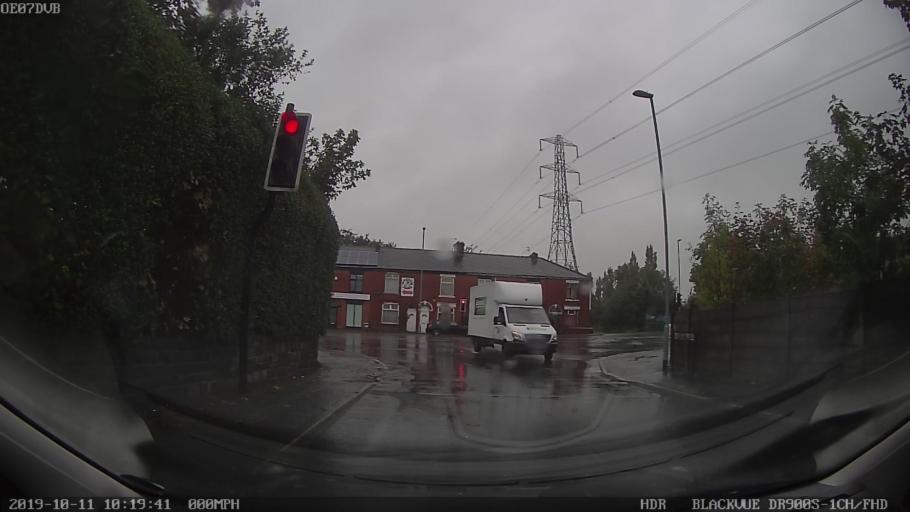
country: GB
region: England
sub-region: Borough of Rochdale
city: Middleton
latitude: 53.5513
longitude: -2.1697
